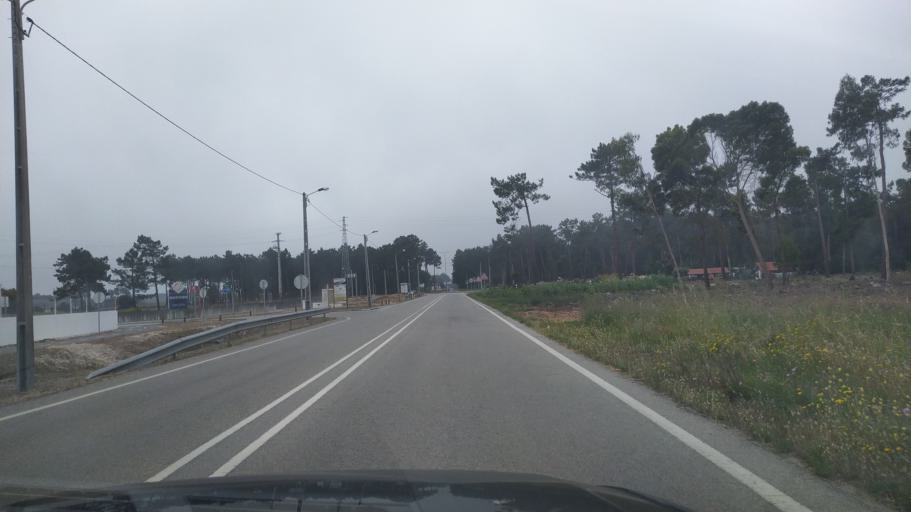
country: PT
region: Aveiro
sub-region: Ilhavo
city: Gafanha da Encarnacao
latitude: 40.6083
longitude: -8.7213
